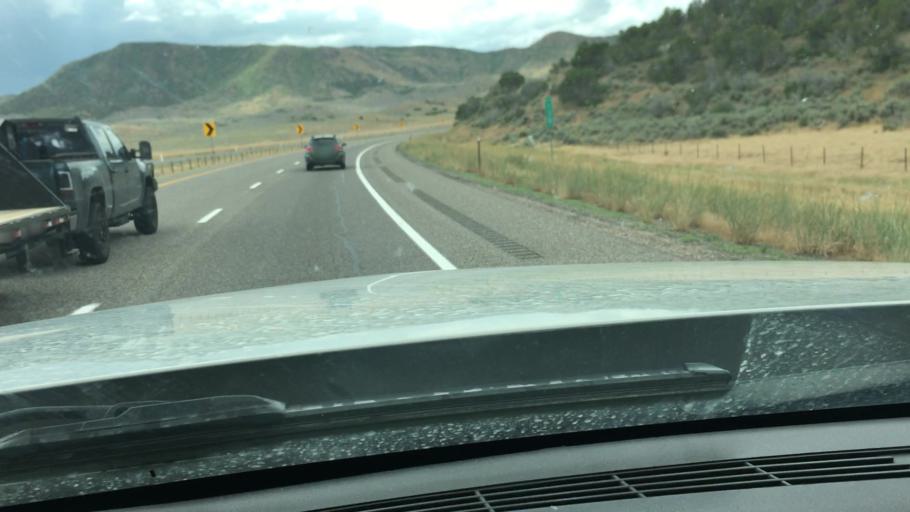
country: US
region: Utah
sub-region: Millard County
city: Fillmore
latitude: 38.6720
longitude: -112.5891
